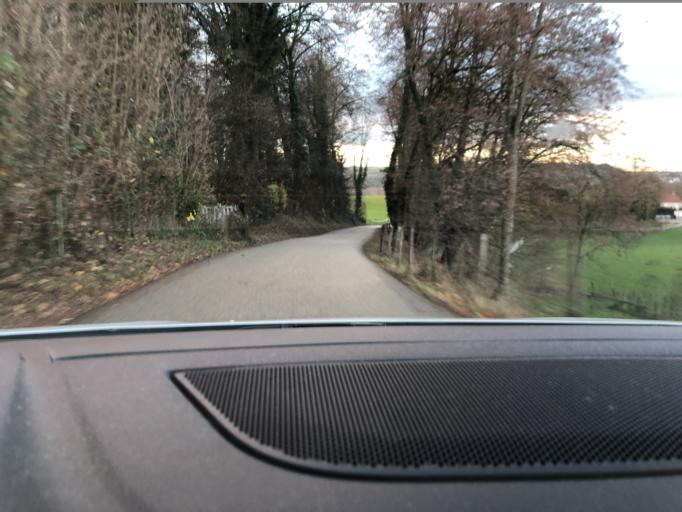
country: FR
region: Rhone-Alpes
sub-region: Departement de l'Isere
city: Fitilieu
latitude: 45.5239
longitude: 5.5557
